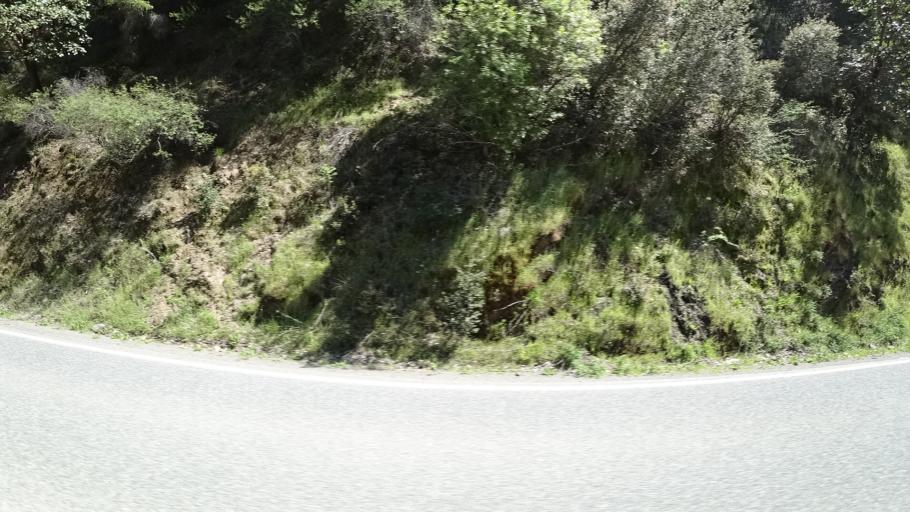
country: US
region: California
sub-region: Trinity County
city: Hayfork
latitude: 40.7752
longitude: -123.3110
